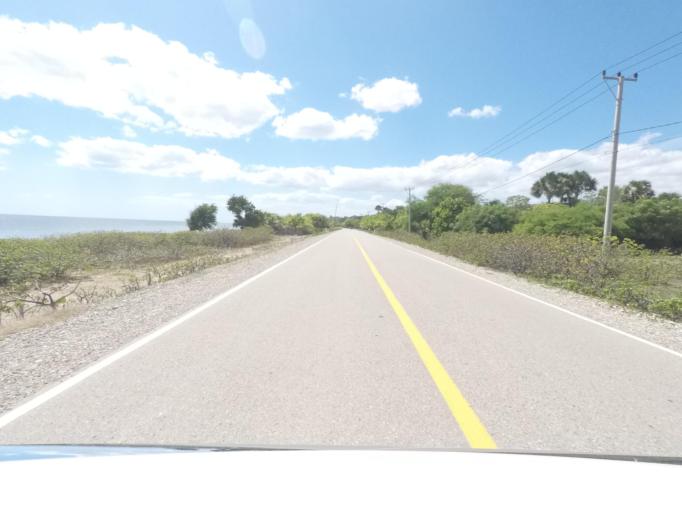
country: TL
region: Baucau
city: Baucau
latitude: -8.4516
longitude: 126.6364
